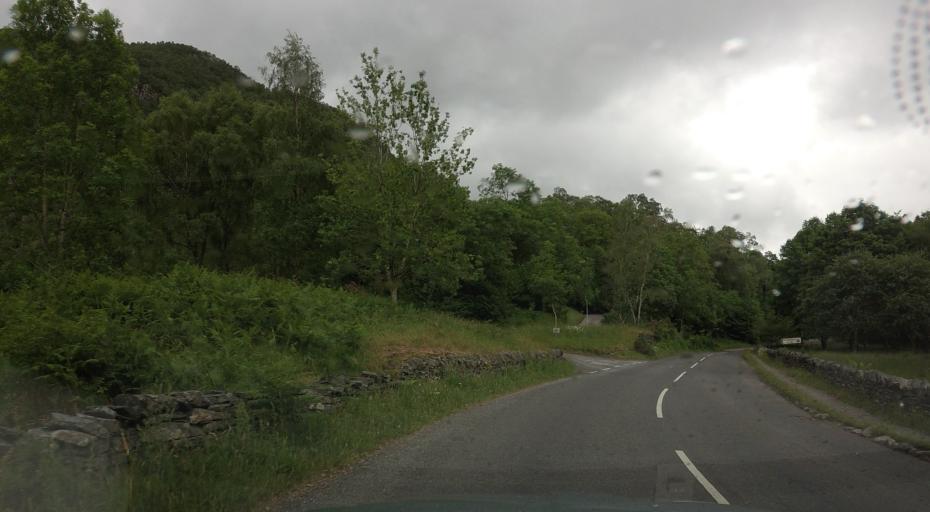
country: GB
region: England
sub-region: Cumbria
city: Keswick
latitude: 54.5419
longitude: -3.1562
